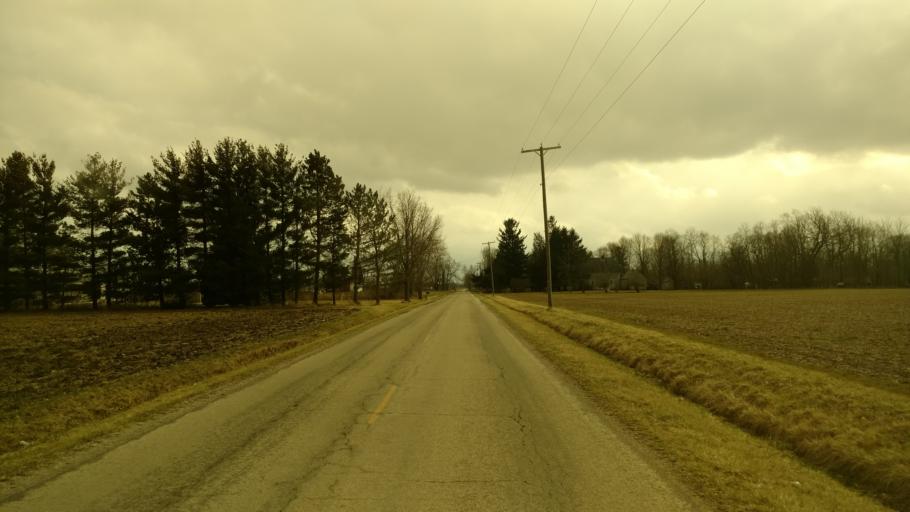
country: US
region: Ohio
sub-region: Crawford County
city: Crestline
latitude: 40.8248
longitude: -82.6965
